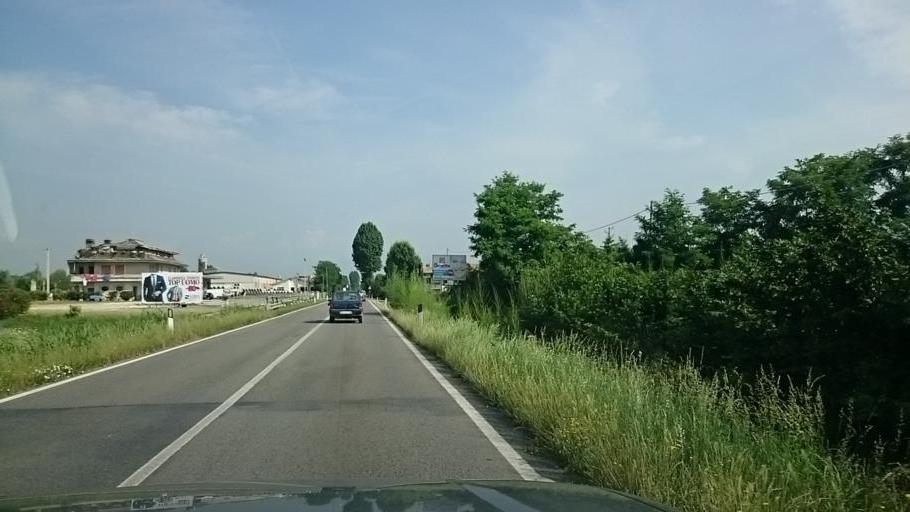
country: IT
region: Veneto
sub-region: Provincia di Treviso
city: Resana
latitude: 45.6441
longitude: 11.9493
